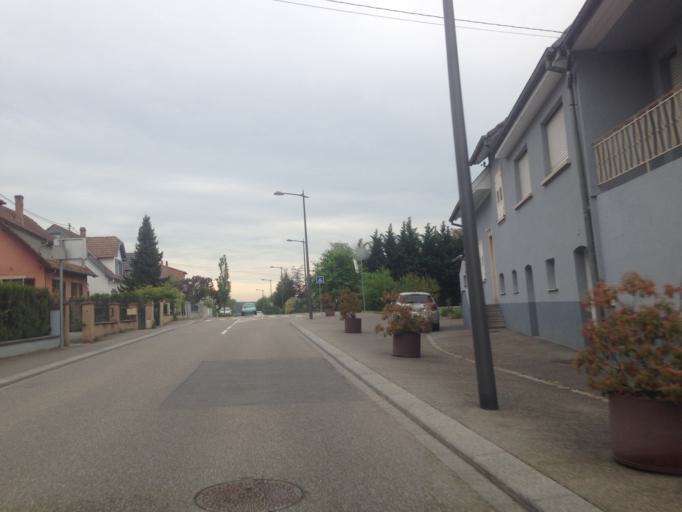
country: FR
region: Alsace
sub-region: Departement du Bas-Rhin
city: Hochfelden
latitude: 48.7637
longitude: 7.5747
